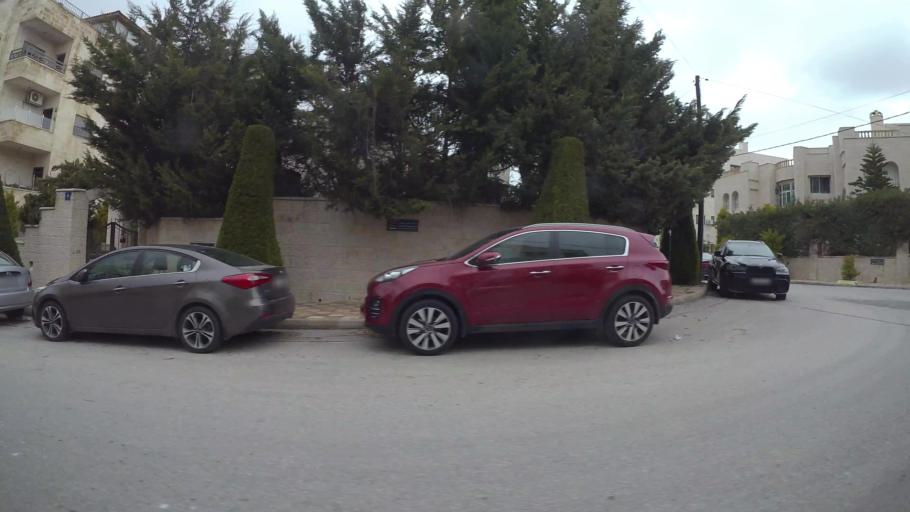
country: JO
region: Amman
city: Wadi as Sir
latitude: 31.9898
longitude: 35.8392
